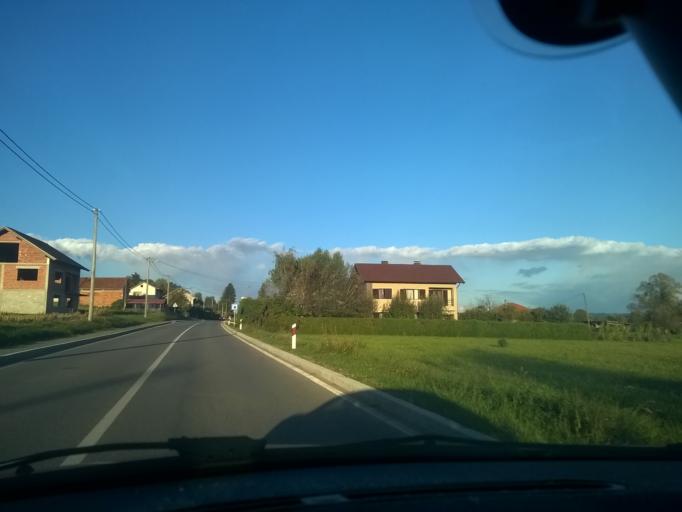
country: HR
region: Zagrebacka
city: Jakovlje
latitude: 46.0037
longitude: 15.8459
